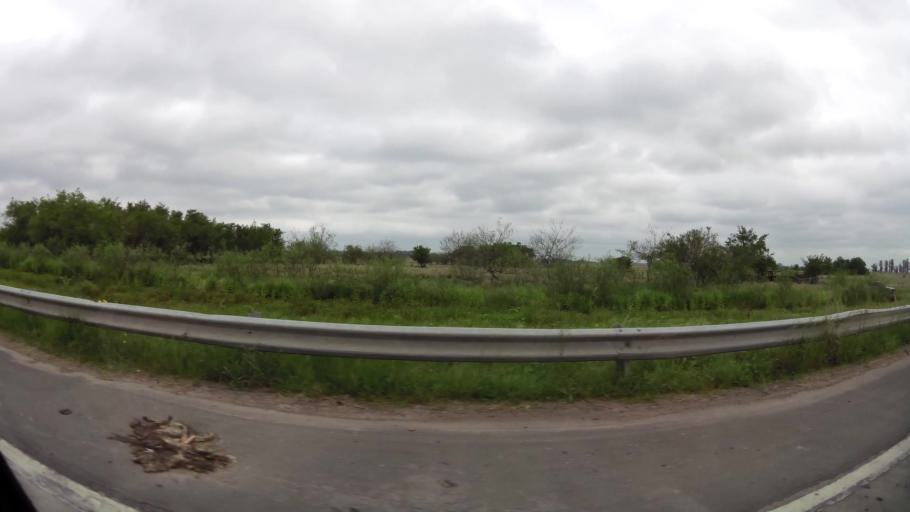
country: AR
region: Buenos Aires
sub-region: Partido de Brandsen
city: Brandsen
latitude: -35.0473
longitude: -58.1419
